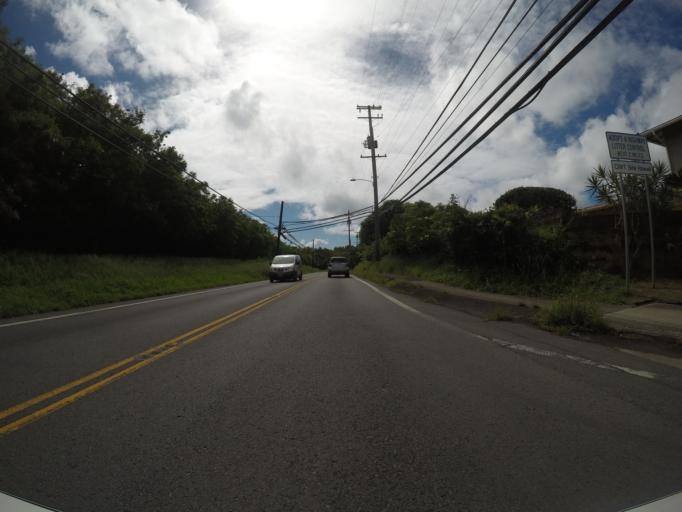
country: US
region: Hawaii
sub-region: Honolulu County
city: Waimanalo
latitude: 21.3466
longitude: -157.7131
